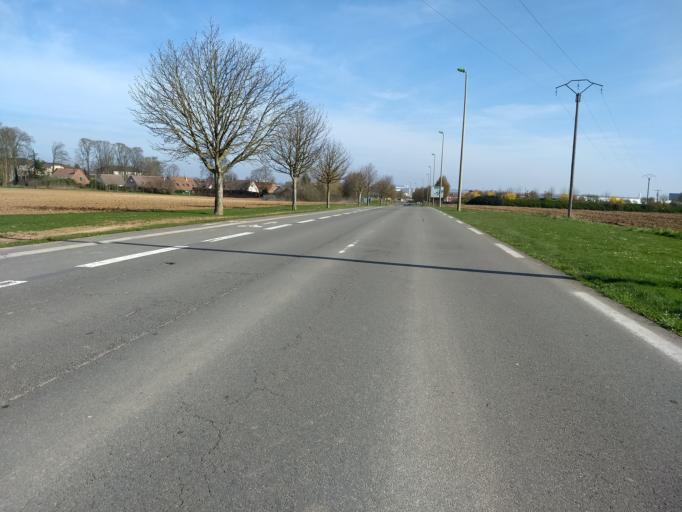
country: FR
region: Nord-Pas-de-Calais
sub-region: Departement du Pas-de-Calais
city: Tilloy-les-Mofflaines
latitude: 50.2798
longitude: 2.8009
